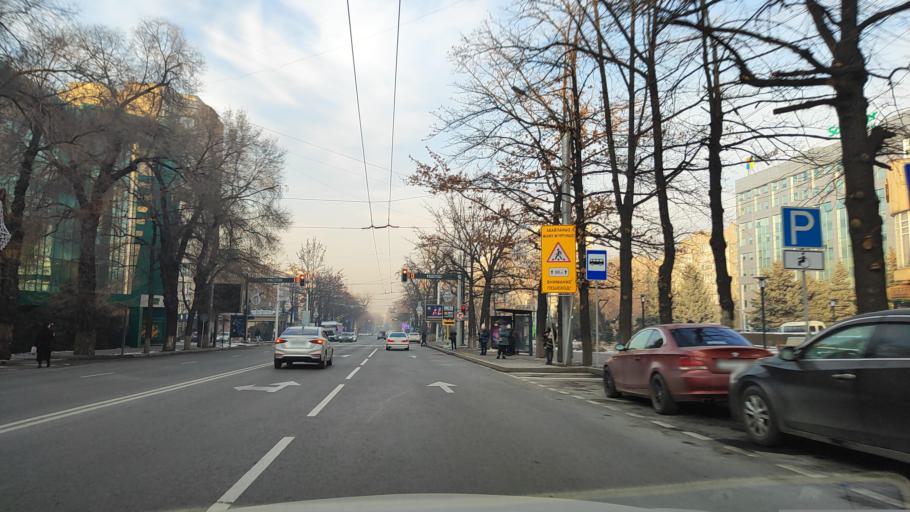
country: KZ
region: Almaty Qalasy
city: Almaty
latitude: 43.2514
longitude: 76.9559
